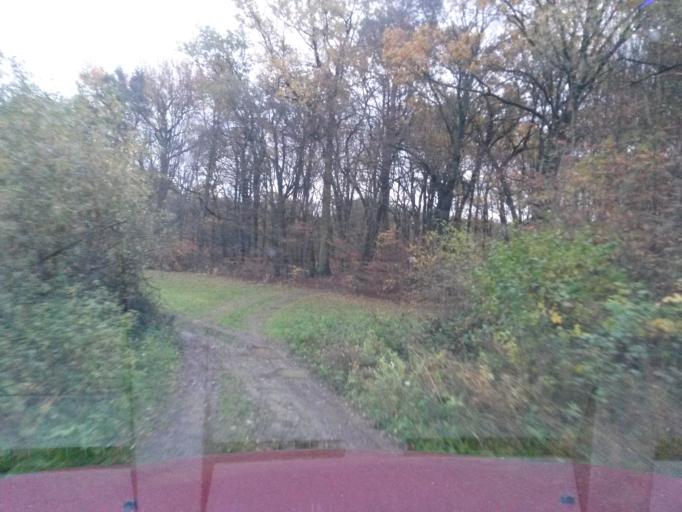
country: SK
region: Kosicky
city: Kosice
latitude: 48.7952
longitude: 21.2873
